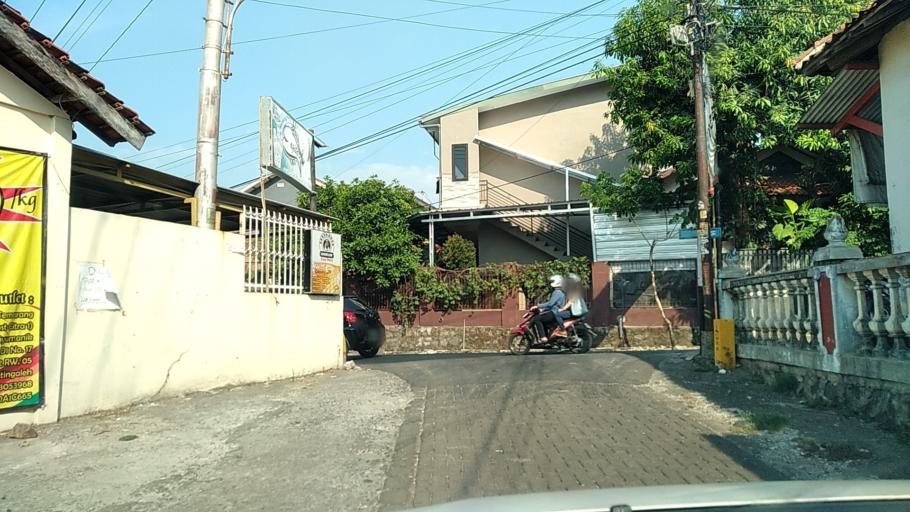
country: ID
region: Central Java
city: Semarang
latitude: -7.0659
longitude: 110.4273
